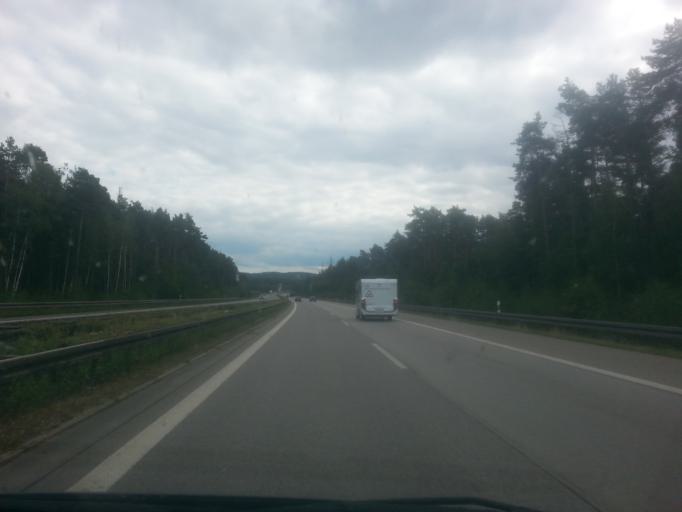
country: DE
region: Bavaria
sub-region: Upper Palatinate
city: Teublitz
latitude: 49.2546
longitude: 12.1245
